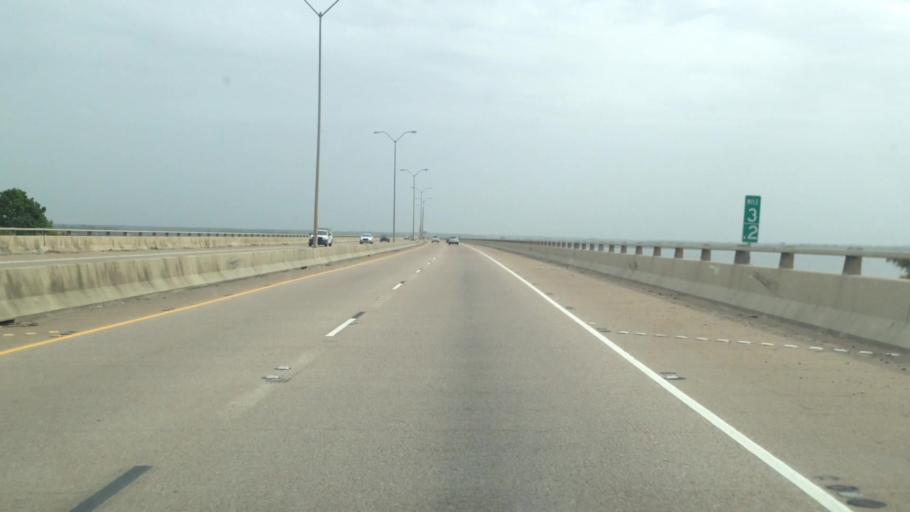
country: US
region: Louisiana
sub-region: Caddo Parish
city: Shreveport
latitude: 32.4966
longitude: -93.8204
